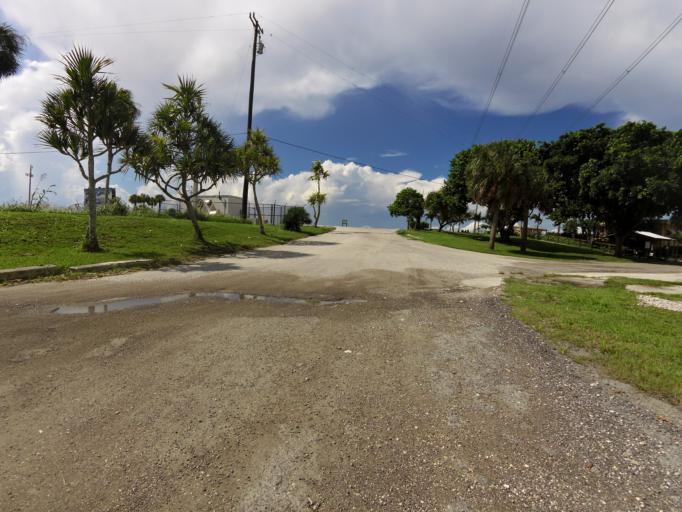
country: US
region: Florida
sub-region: Broward County
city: Weston
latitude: 26.1761
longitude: -80.4478
